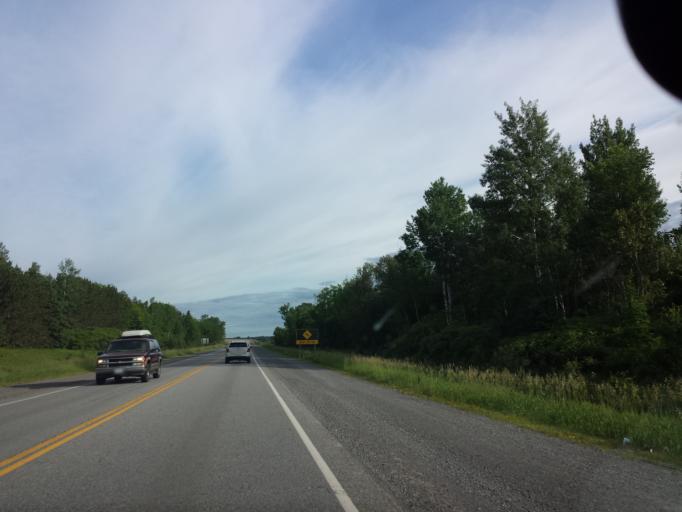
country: CA
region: Ontario
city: Renfrew
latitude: 45.4717
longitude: -76.6256
